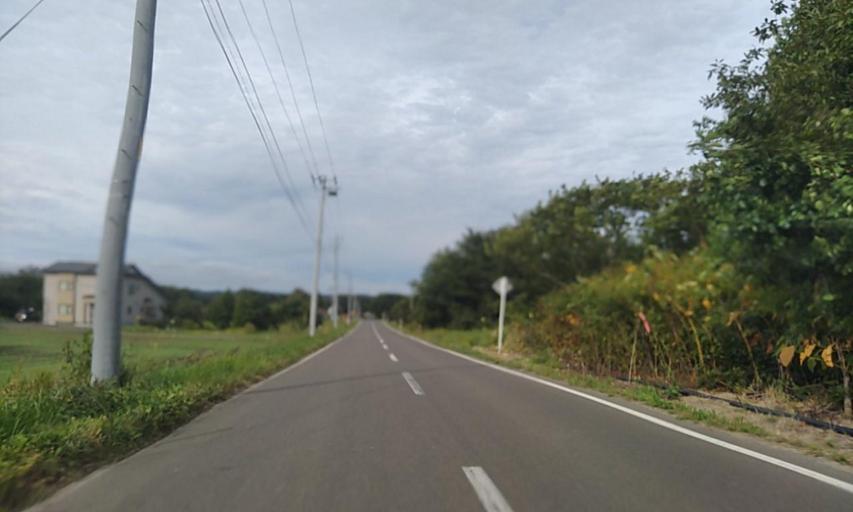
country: JP
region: Hokkaido
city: Abashiri
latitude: 43.7957
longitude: 144.5609
